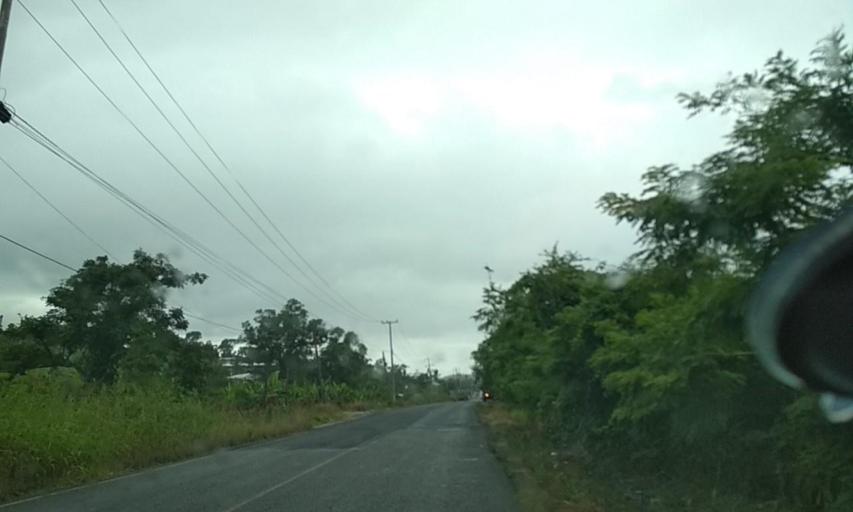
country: MX
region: Veracruz
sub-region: Papantla
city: Residencial Tajin
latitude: 20.6380
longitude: -97.3687
